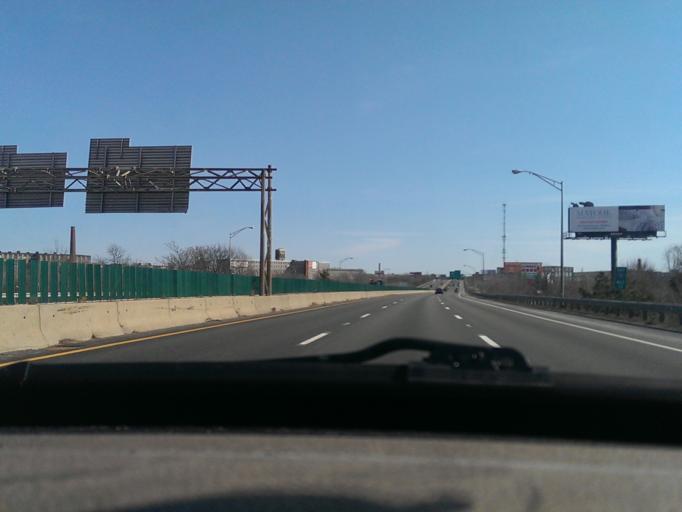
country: US
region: Massachusetts
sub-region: Bristol County
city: Fall River
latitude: 41.6939
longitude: -71.1463
